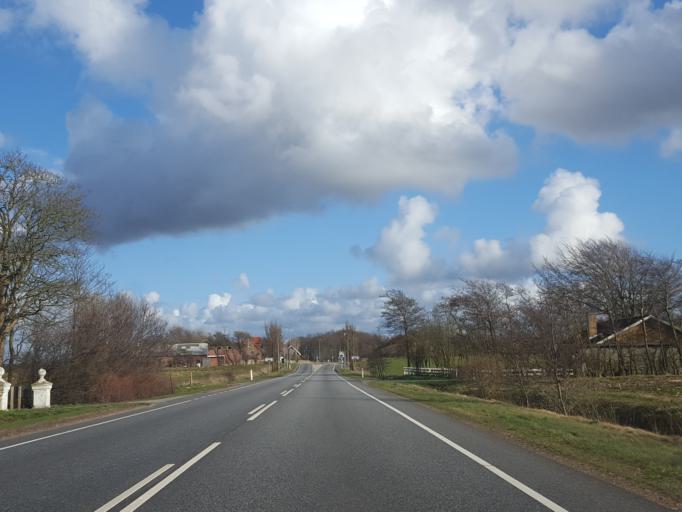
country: DK
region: South Denmark
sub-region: Esbjerg Kommune
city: Tjaereborg
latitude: 55.4892
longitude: 8.6360
